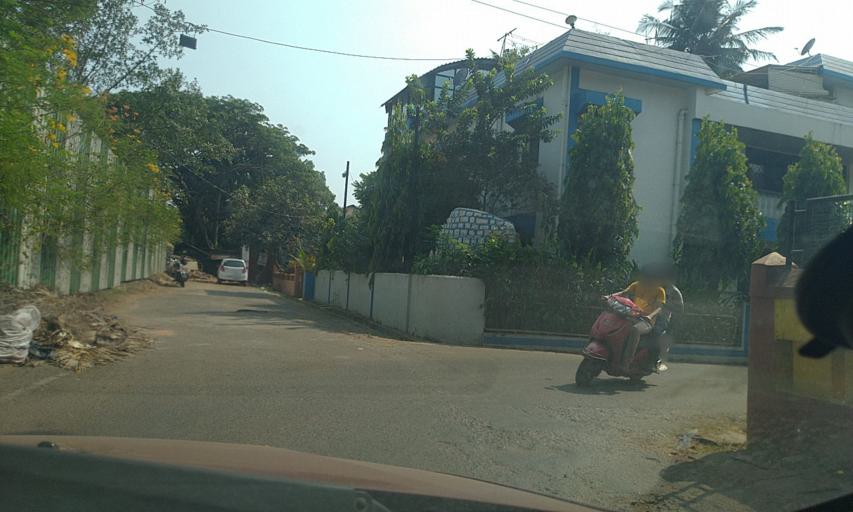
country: IN
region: Goa
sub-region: North Goa
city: Panaji
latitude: 15.4872
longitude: 73.8164
